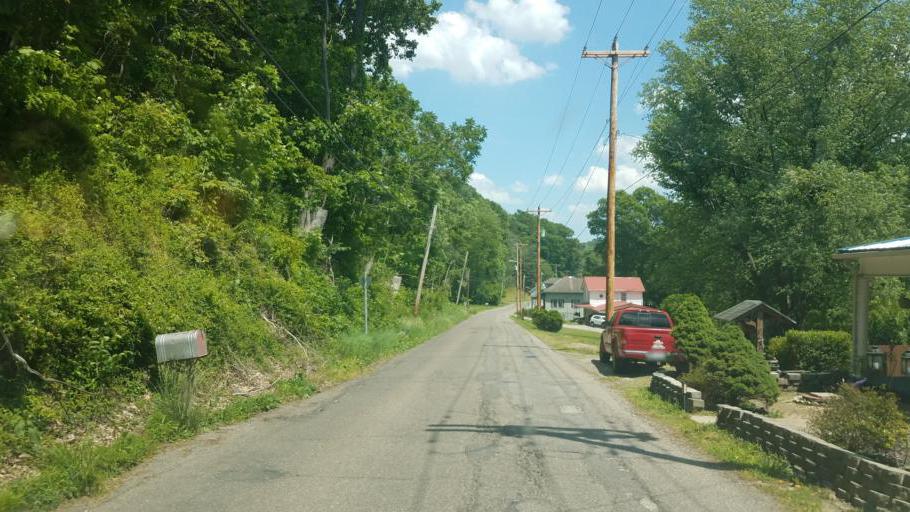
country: US
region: Ohio
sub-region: Meigs County
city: Pomeroy
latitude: 39.0326
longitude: -82.0484
